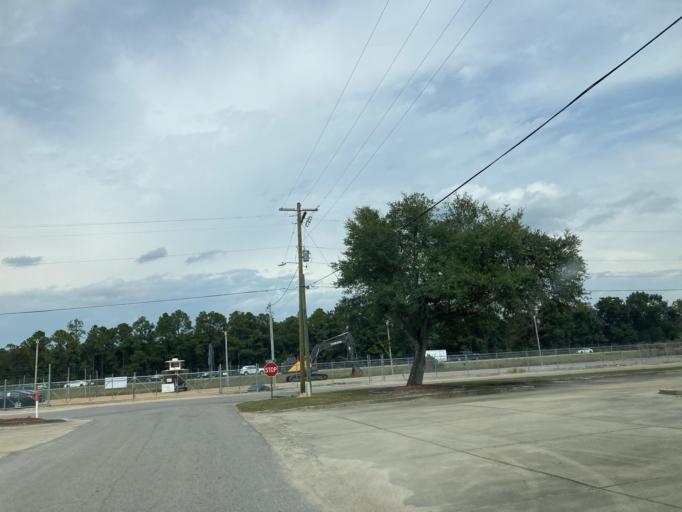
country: US
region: Mississippi
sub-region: Jackson County
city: Saint Martin
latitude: 30.4530
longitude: -88.8498
